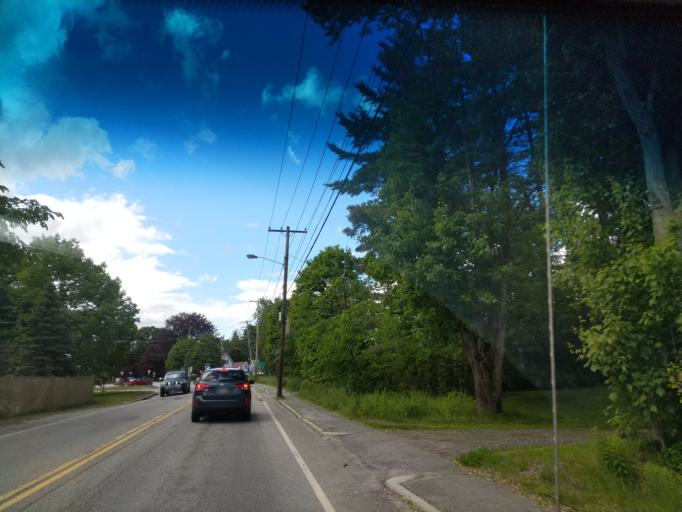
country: US
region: Maine
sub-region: Cumberland County
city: South Windham
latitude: 43.7276
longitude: -70.4242
